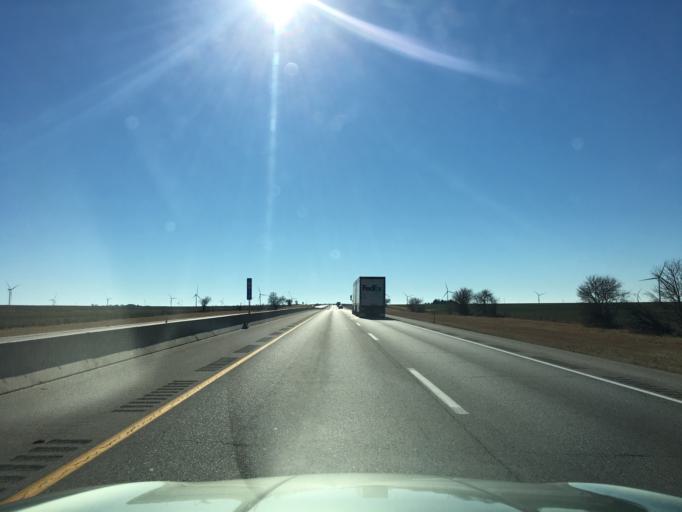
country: US
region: Kansas
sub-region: Sumner County
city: Wellington
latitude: 37.1702
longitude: -97.3396
